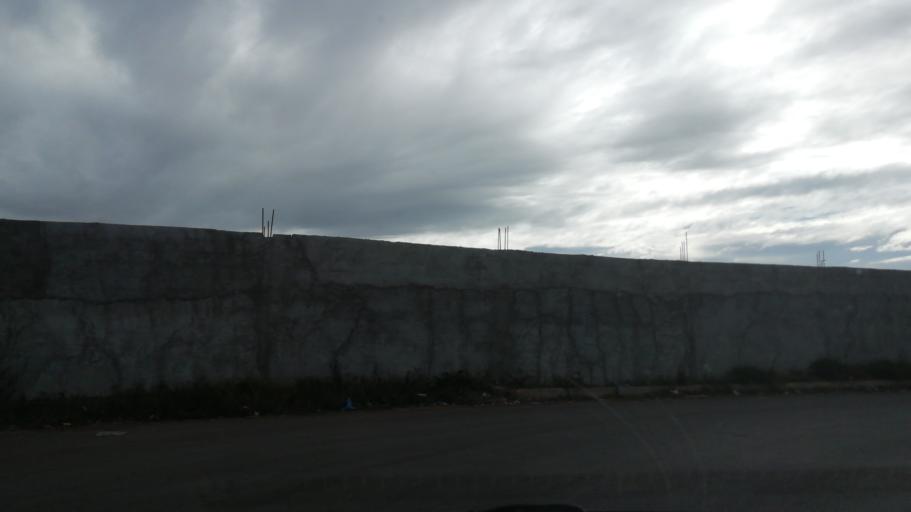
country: DZ
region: Oran
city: Oran
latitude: 35.6921
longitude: -0.5967
